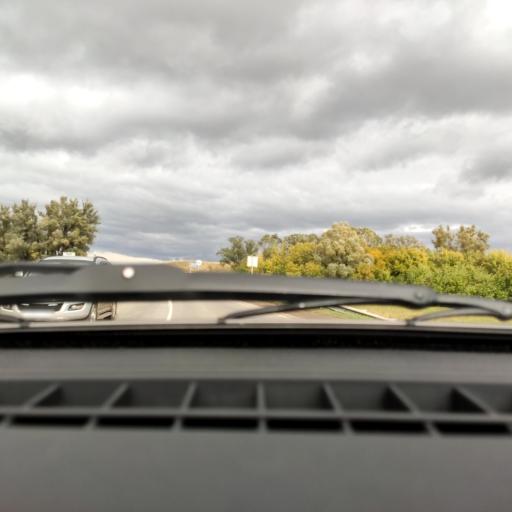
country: RU
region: Bashkortostan
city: Rayevskiy
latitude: 54.0139
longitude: 54.8744
